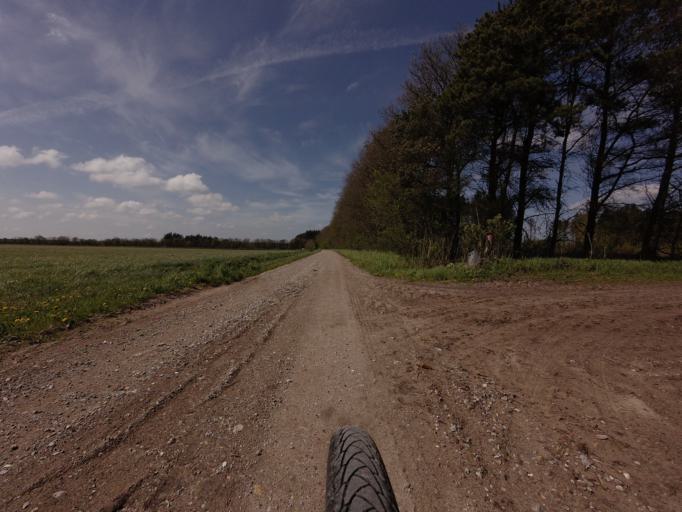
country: DK
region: North Denmark
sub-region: Jammerbugt Kommune
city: Brovst
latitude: 57.1553
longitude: 9.5672
